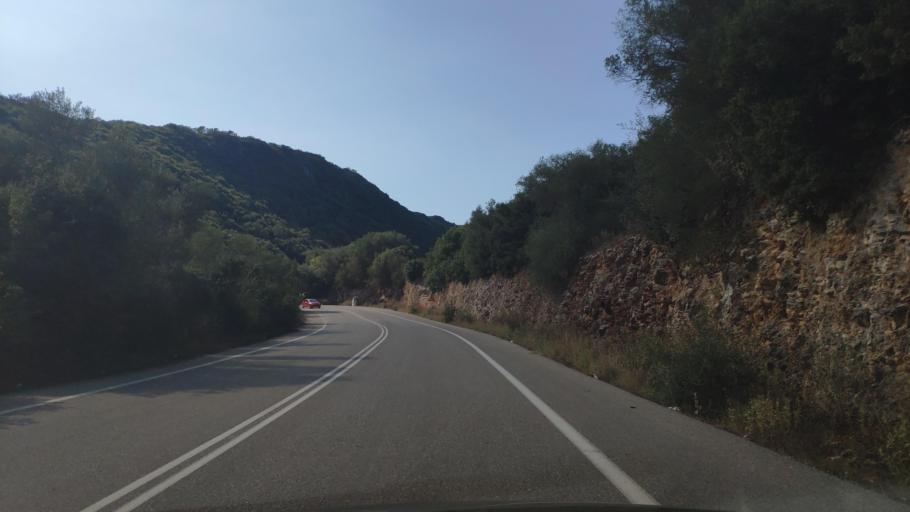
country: GR
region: West Greece
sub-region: Nomos Aitolias kai Akarnanias
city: Stanos
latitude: 38.7766
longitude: 21.1492
